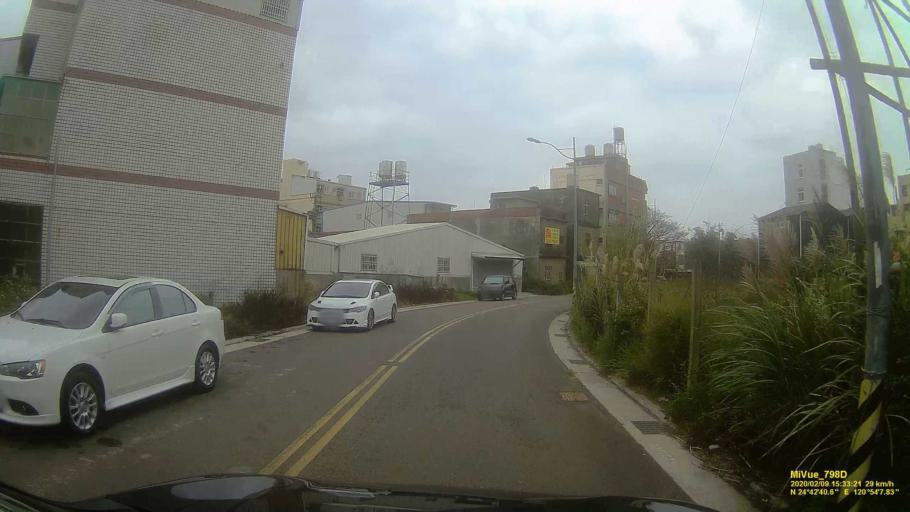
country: TW
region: Taiwan
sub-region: Hsinchu
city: Hsinchu
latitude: 24.7113
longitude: 120.9021
